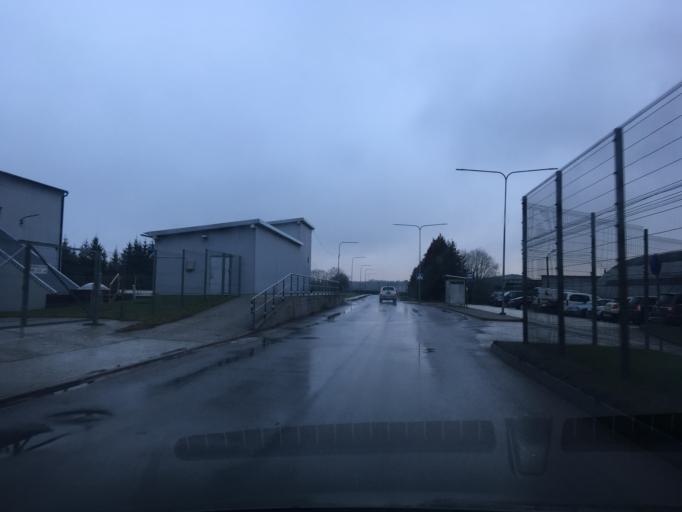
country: EE
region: Tartu
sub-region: Tartu linn
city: Tartu
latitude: 58.3704
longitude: 26.7918
